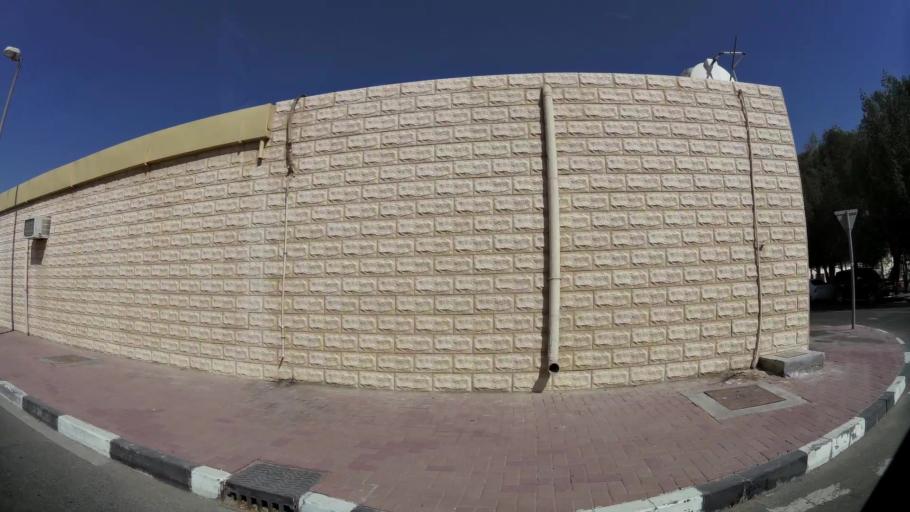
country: AE
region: Ash Shariqah
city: Sharjah
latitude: 25.2421
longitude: 55.2947
